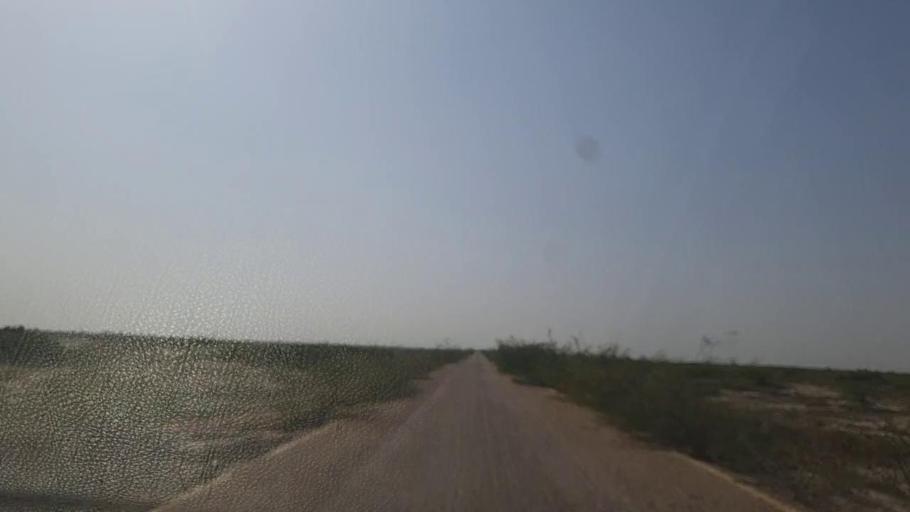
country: PK
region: Sindh
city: Naukot
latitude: 24.5924
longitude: 69.2980
